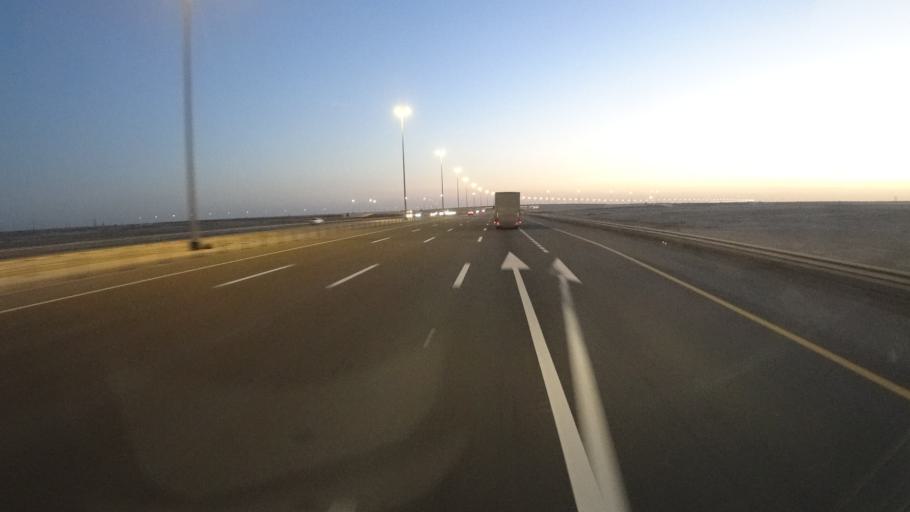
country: AE
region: Dubai
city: Dubai
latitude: 24.7727
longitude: 54.9515
